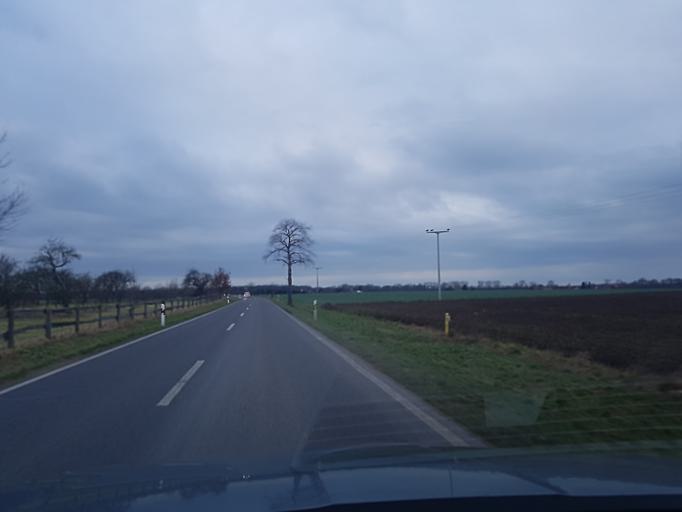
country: DE
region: Brandenburg
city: Sonnewalde
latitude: 51.6925
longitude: 13.6673
